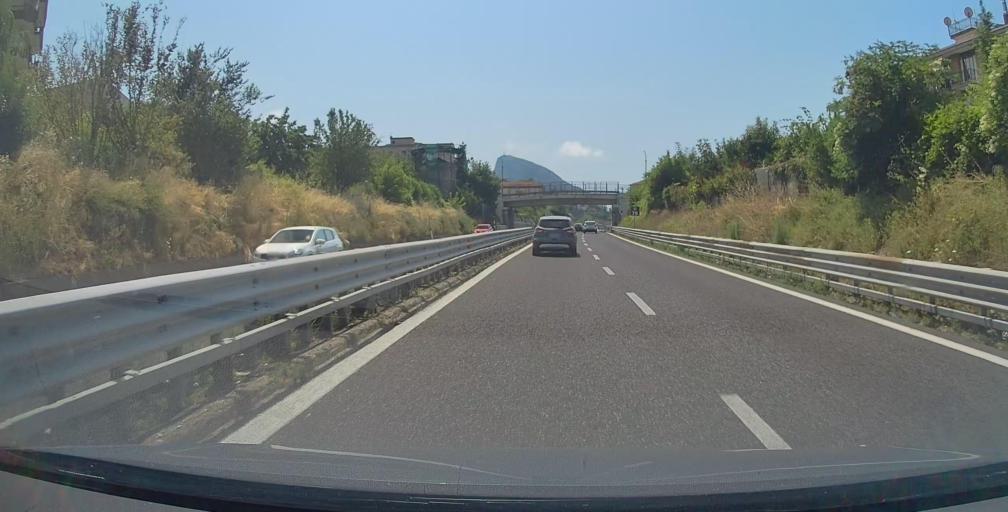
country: IT
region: Campania
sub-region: Provincia di Salerno
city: Cava De Tirreni
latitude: 40.6994
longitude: 14.7133
